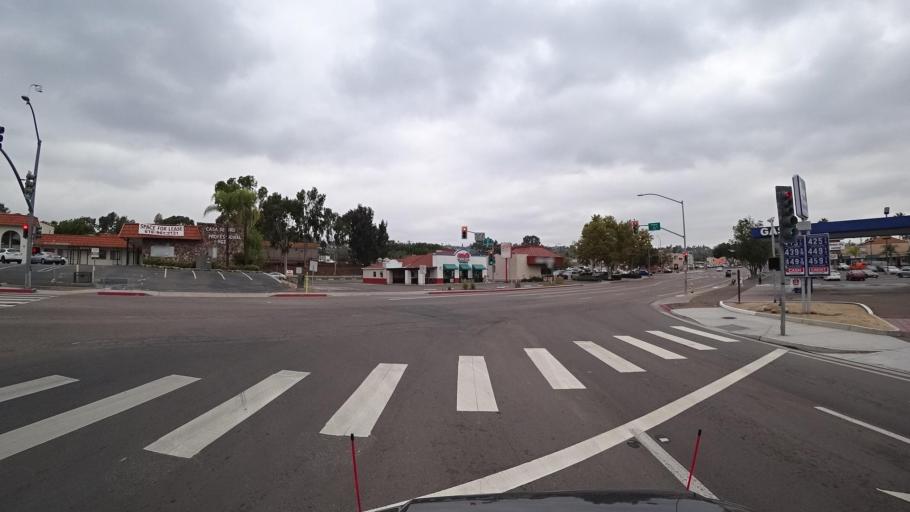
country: US
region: California
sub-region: San Diego County
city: Spring Valley
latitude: 32.7478
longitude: -116.9885
